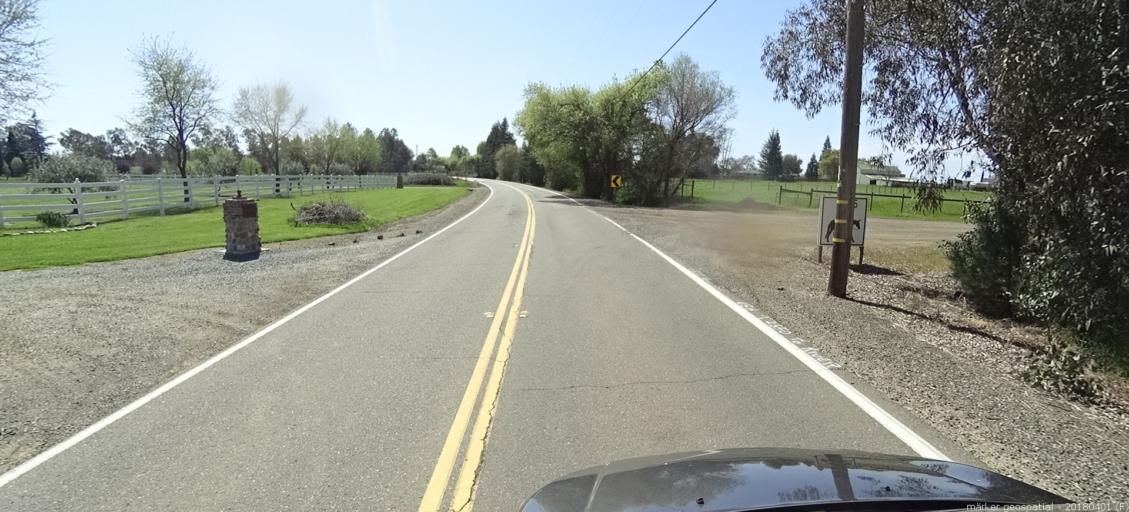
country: US
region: California
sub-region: Sacramento County
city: Wilton
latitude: 38.4183
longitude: -121.2510
